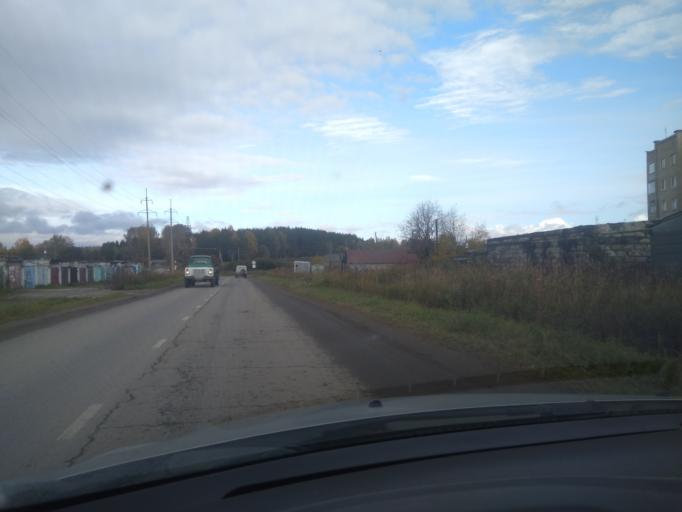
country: RU
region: Sverdlovsk
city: Nikolo-Pavlovskoye
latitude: 57.7992
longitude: 60.0488
